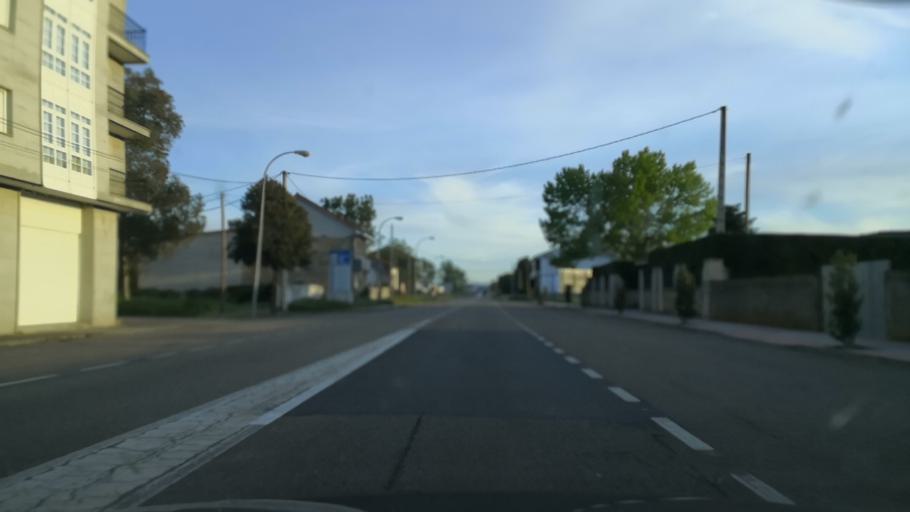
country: ES
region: Galicia
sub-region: Provincia de Ourense
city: Verin
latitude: 41.9312
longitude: -7.4405
